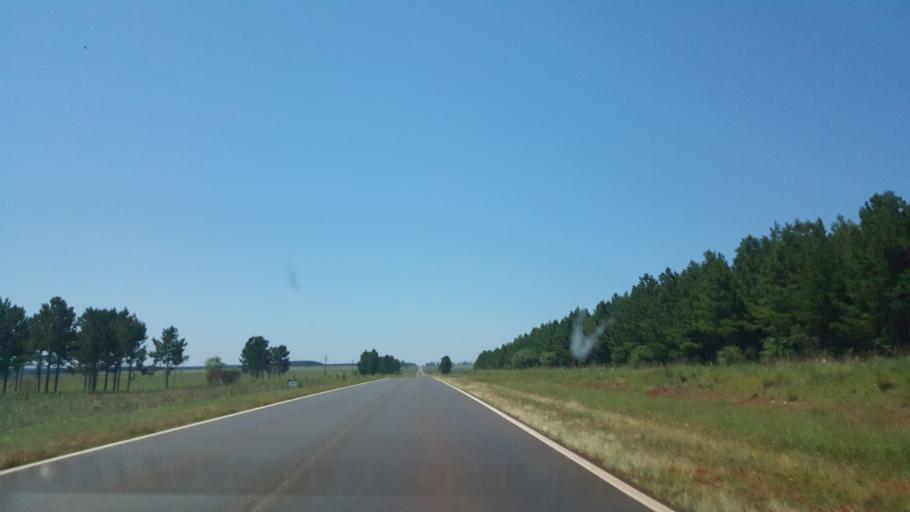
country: AR
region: Corrientes
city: Santo Tome
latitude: -28.3907
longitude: -56.1076
